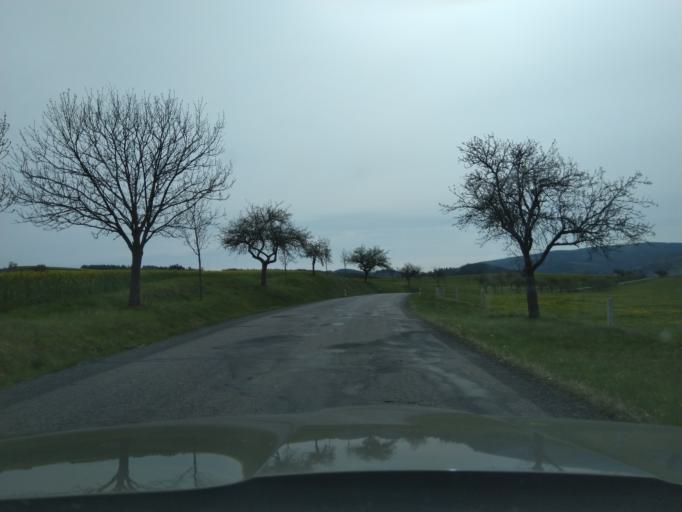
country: CZ
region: Plzensky
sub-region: Okres Klatovy
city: Kasperske Hory
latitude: 49.2017
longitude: 13.6136
